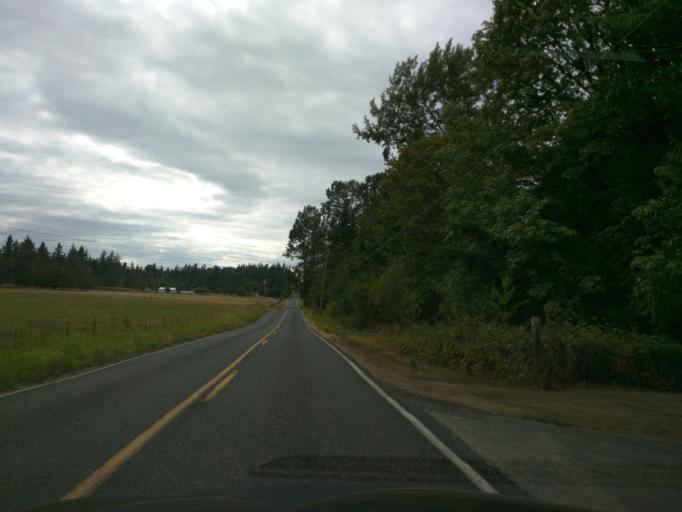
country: US
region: Washington
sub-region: Whatcom County
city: Bellingham
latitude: 48.8147
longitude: -122.4482
